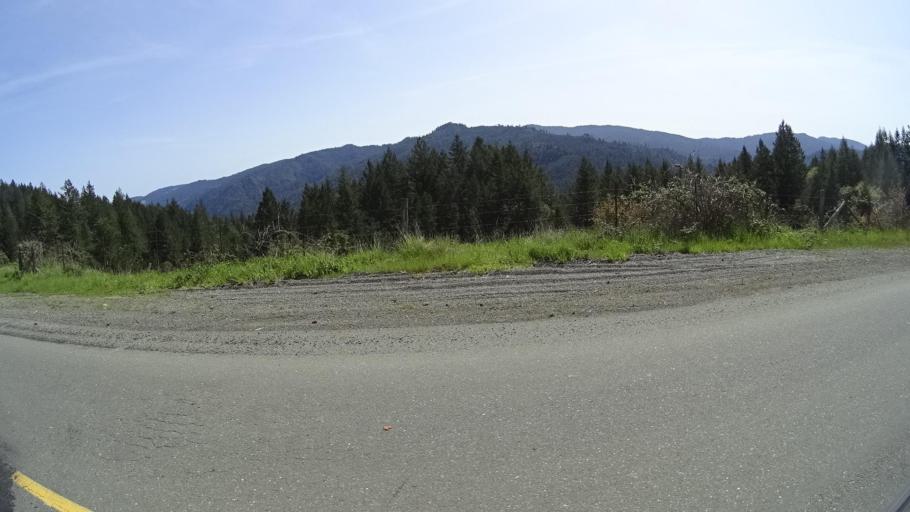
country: US
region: California
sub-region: Humboldt County
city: Redway
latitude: 40.4139
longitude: -123.7599
